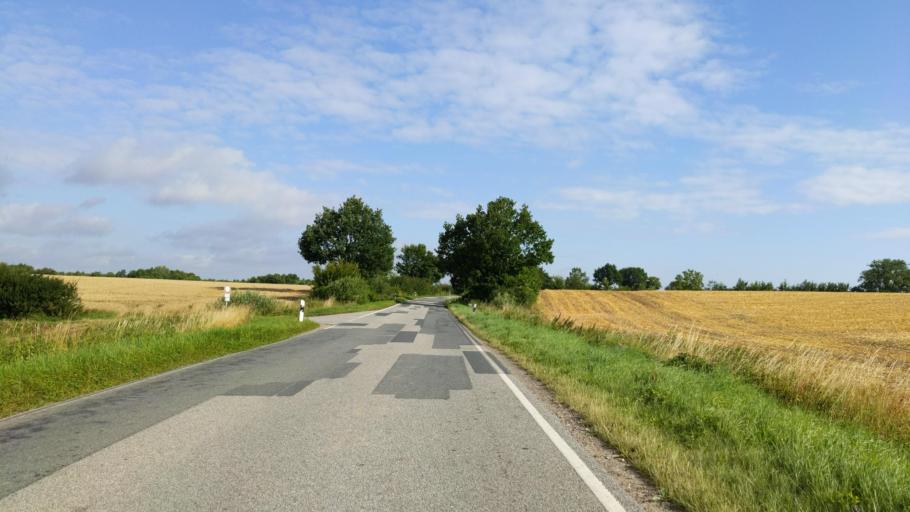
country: DE
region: Schleswig-Holstein
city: Bad Schwartau
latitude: 53.9725
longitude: 10.6559
